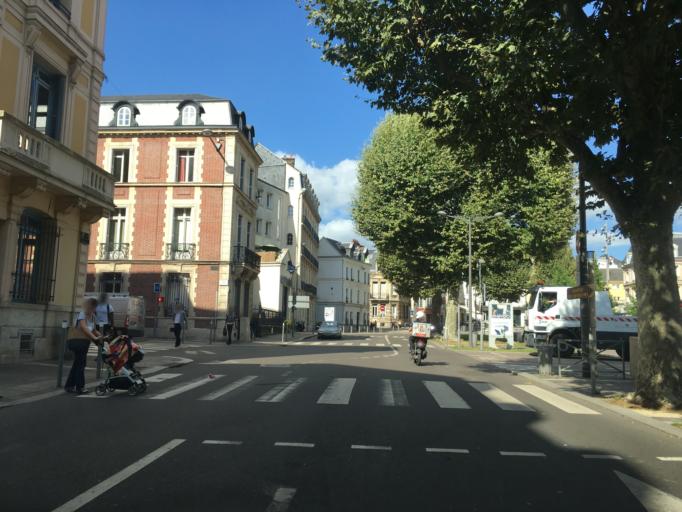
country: FR
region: Haute-Normandie
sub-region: Departement de la Seine-Maritime
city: Rouen
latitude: 49.4433
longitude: 1.0983
